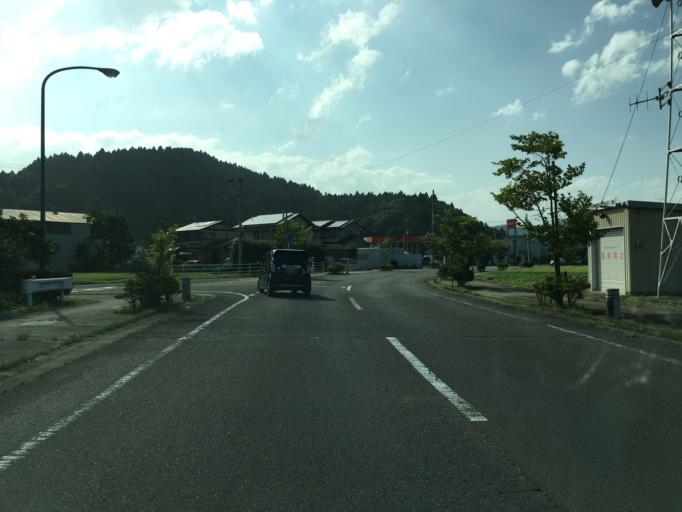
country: JP
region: Miyagi
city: Marumori
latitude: 37.9260
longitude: 140.7658
